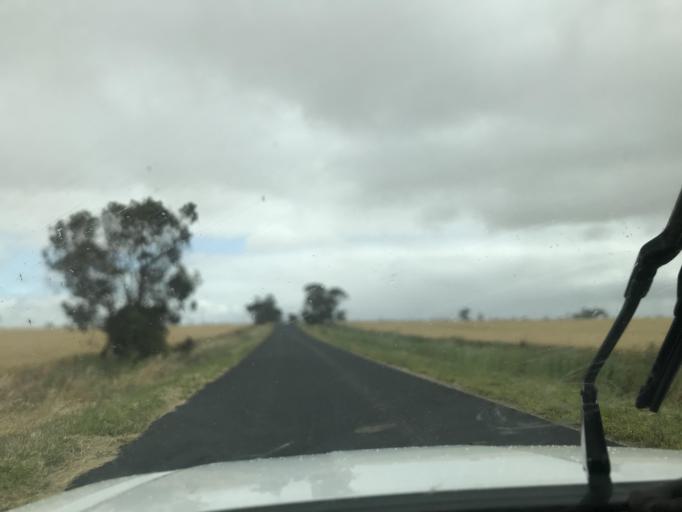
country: AU
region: South Australia
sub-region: Tatiara
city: Bordertown
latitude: -36.2810
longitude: 141.1486
